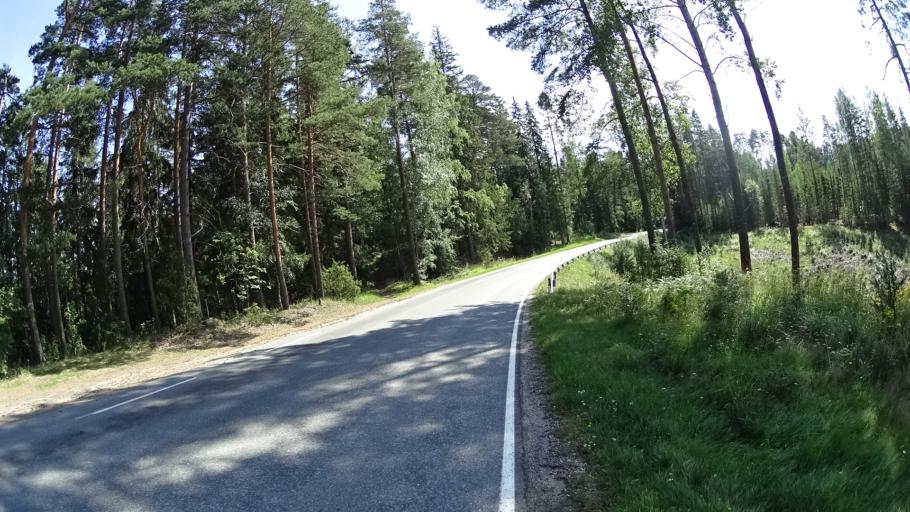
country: FI
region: Haeme
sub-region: Forssa
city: Tammela
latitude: 60.7735
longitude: 23.8454
